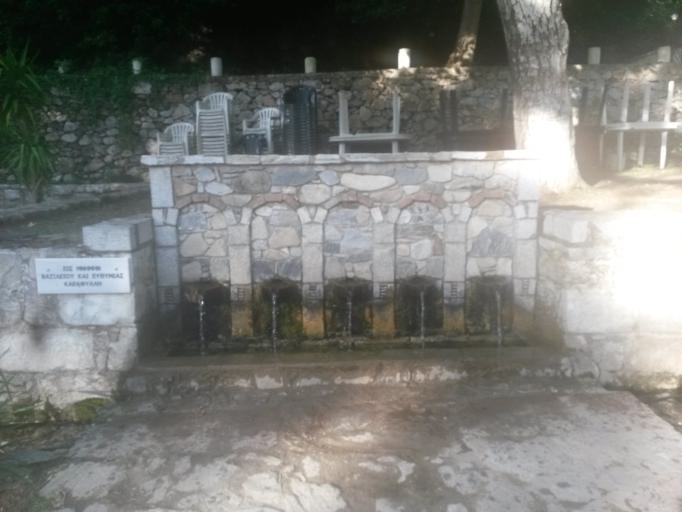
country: GR
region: North Aegean
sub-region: Nomos Lesvou
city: Agiasos
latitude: 39.0963
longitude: 26.4020
